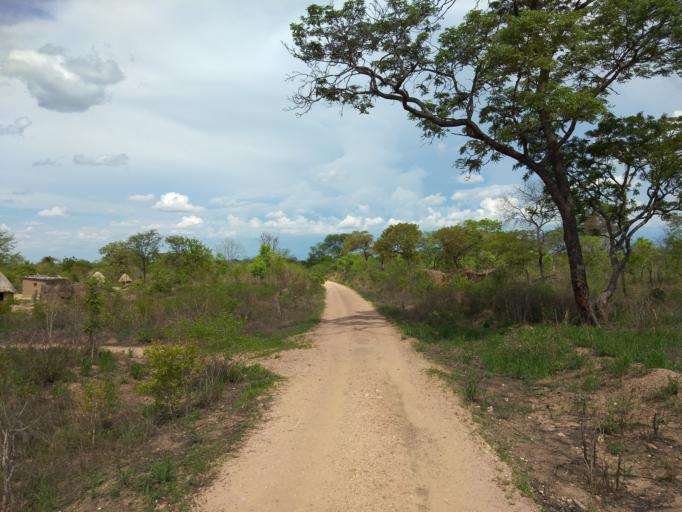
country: ZM
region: Eastern
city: Nyimba
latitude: -14.1148
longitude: 30.1156
